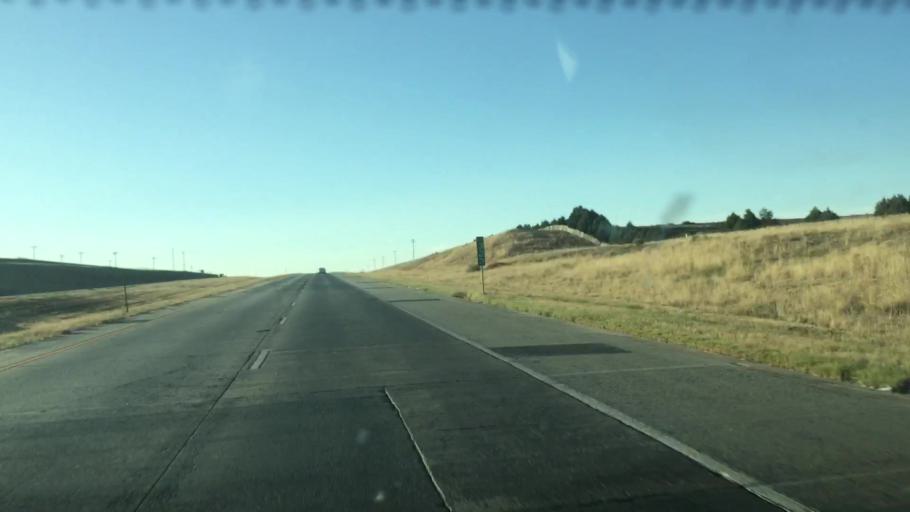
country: US
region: Colorado
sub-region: Arapahoe County
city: Byers
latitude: 39.6739
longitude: -104.1017
